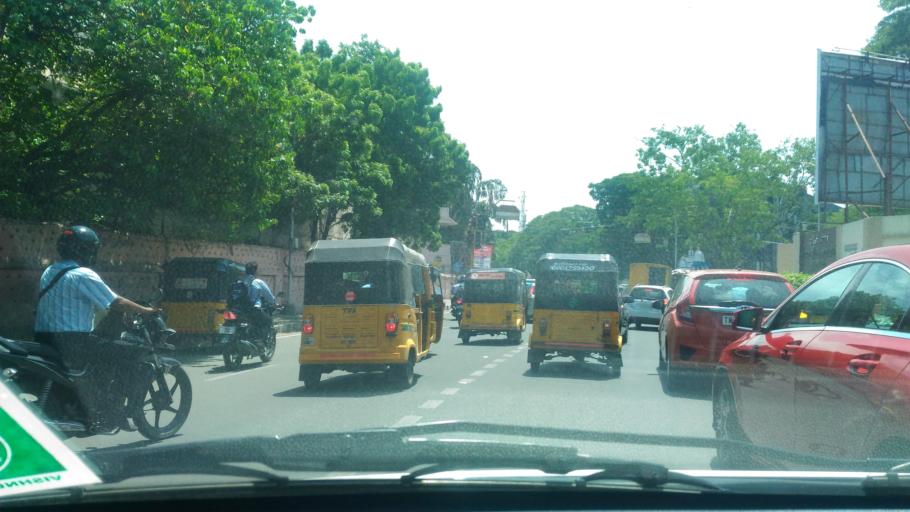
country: IN
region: Tamil Nadu
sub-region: Chennai
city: Chetput
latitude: 13.0493
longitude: 80.2471
